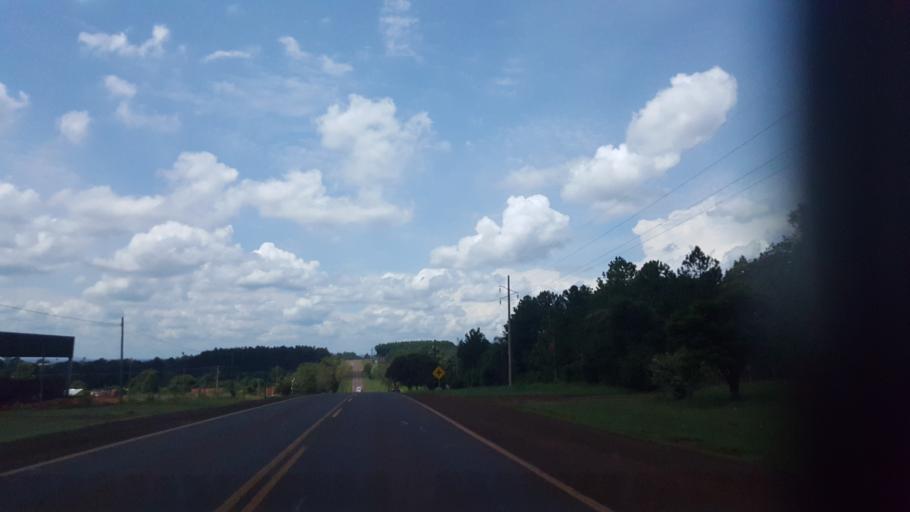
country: AR
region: Misiones
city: Puerto Rico
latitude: -26.8207
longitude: -55.0104
